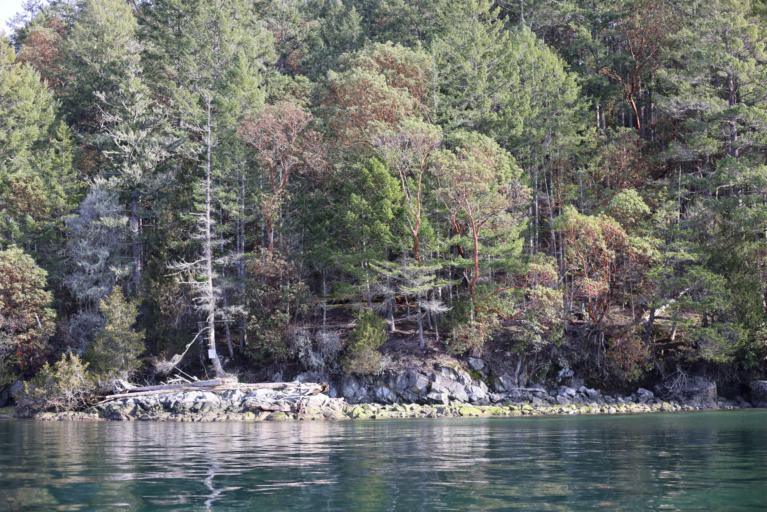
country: CA
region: British Columbia
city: Duncan
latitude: 48.7628
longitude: -123.5952
